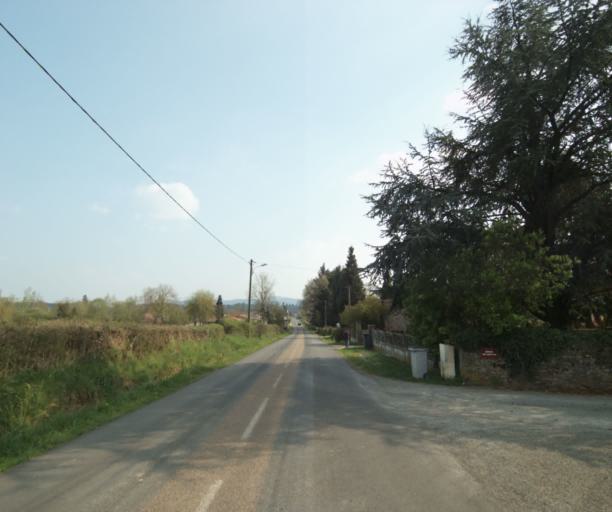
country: FR
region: Bourgogne
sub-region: Departement de Saone-et-Loire
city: Charolles
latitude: 46.4875
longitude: 4.4354
